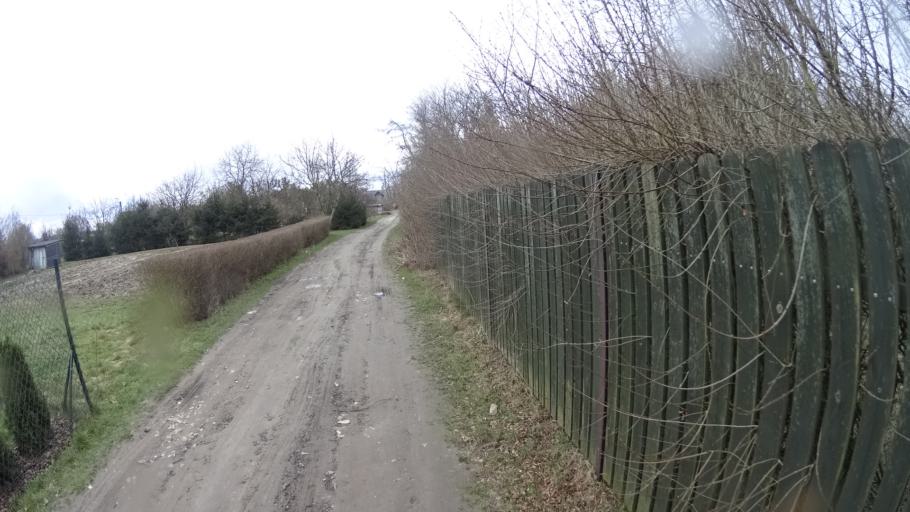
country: PL
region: Masovian Voivodeship
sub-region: Powiat warszawski zachodni
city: Blonie
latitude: 52.2190
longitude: 20.6468
